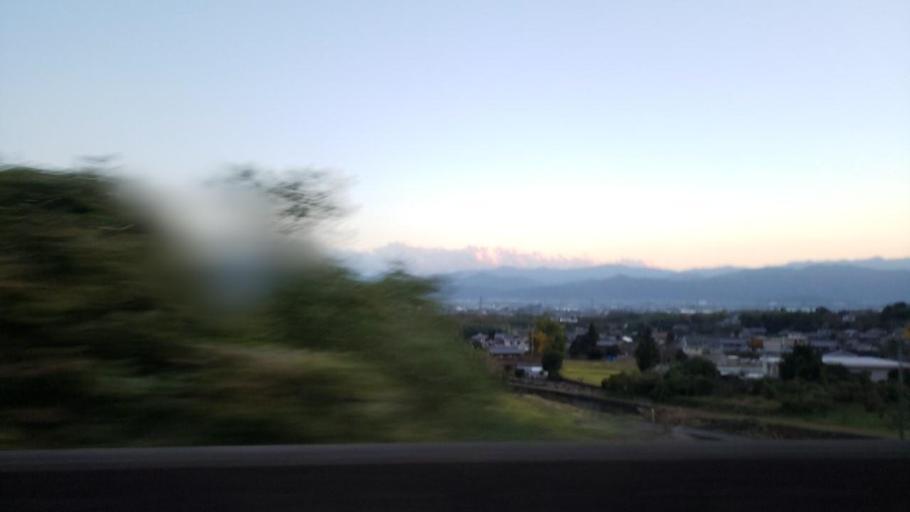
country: JP
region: Tokushima
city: Ishii
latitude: 34.1393
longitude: 134.4048
